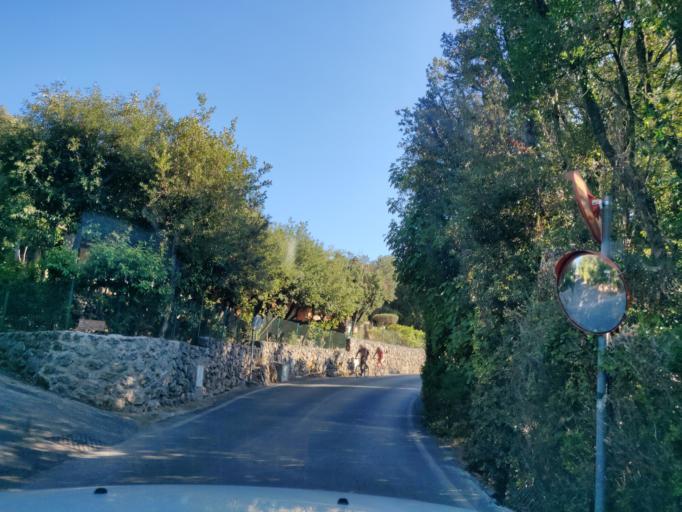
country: IT
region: Tuscany
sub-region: Provincia di Grosseto
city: Orbetello Scalo
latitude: 42.4165
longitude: 11.2825
